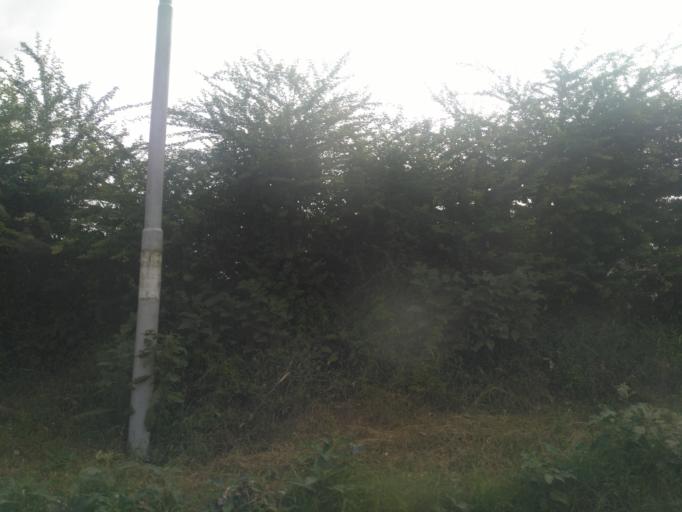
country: TZ
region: Zanzibar Urban/West
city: Zanzibar
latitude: -6.1736
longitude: 39.2036
